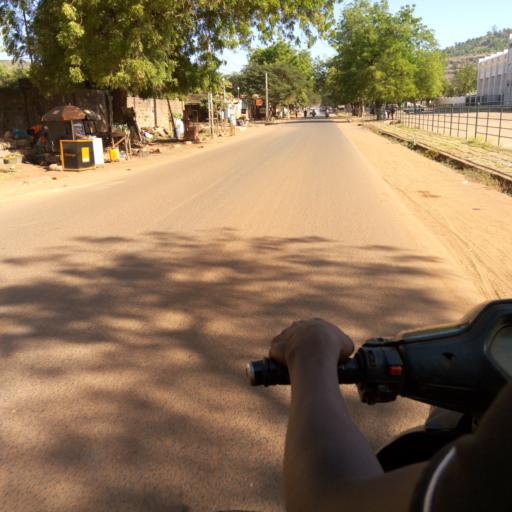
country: ML
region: Bamako
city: Bamako
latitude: 12.6534
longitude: -8.0166
